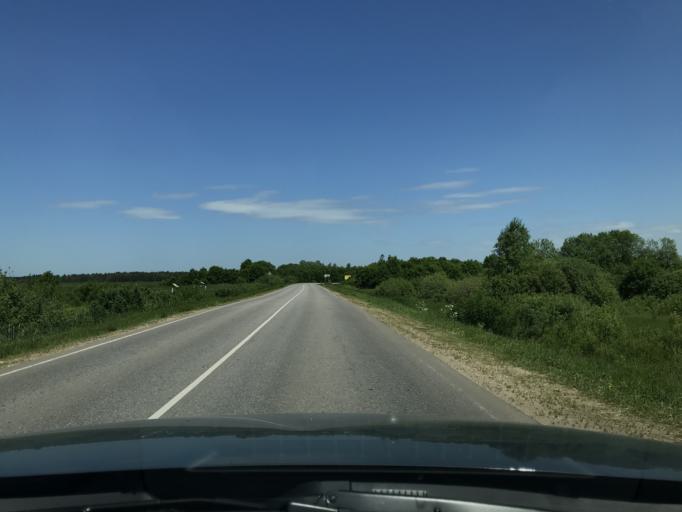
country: RU
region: Moskovskaya
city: Vereya
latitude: 55.3243
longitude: 36.2758
